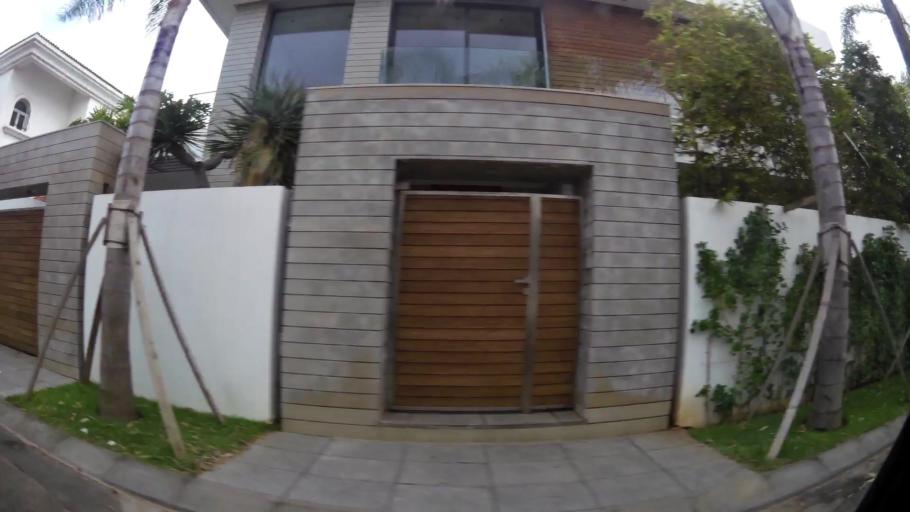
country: MA
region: Grand Casablanca
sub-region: Casablanca
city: Casablanca
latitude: 33.5846
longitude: -7.6846
